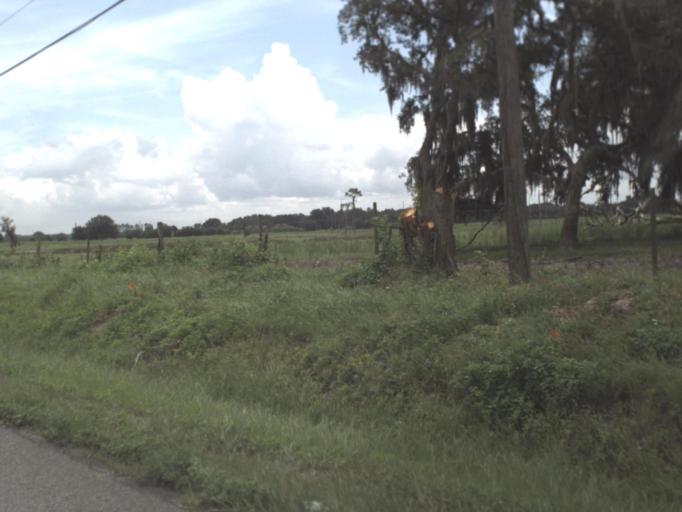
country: US
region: Florida
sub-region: Pasco County
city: San Antonio
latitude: 28.3257
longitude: -82.3184
